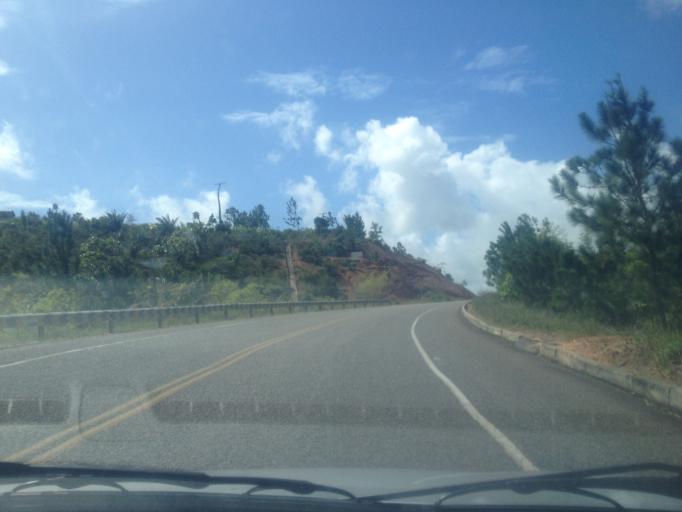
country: BR
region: Bahia
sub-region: Conde
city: Conde
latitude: -11.8809
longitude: -37.6485
